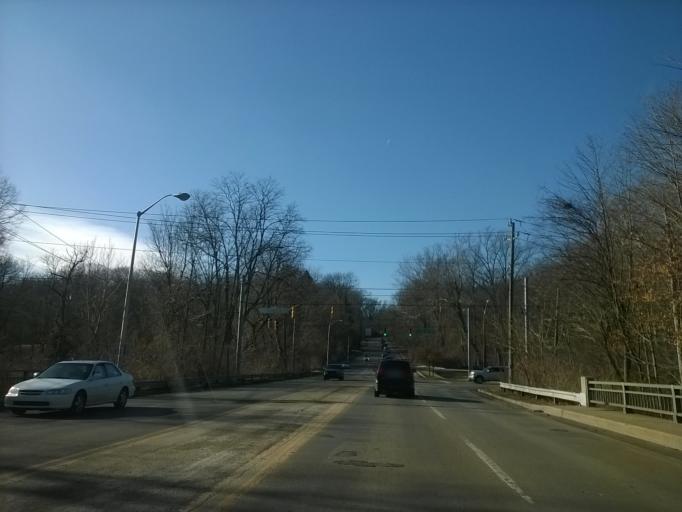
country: US
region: Indiana
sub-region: Marion County
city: Broad Ripple
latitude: 39.8622
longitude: -86.1624
